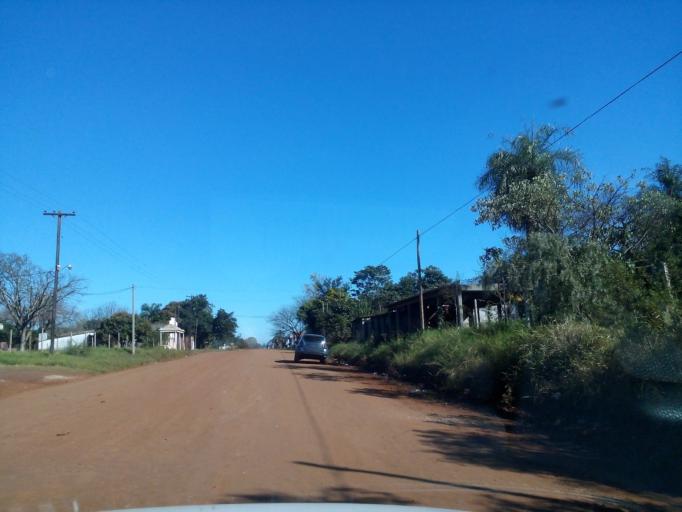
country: AR
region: Misiones
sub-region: Departamento de Capital
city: Posadas
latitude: -27.3765
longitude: -55.9419
